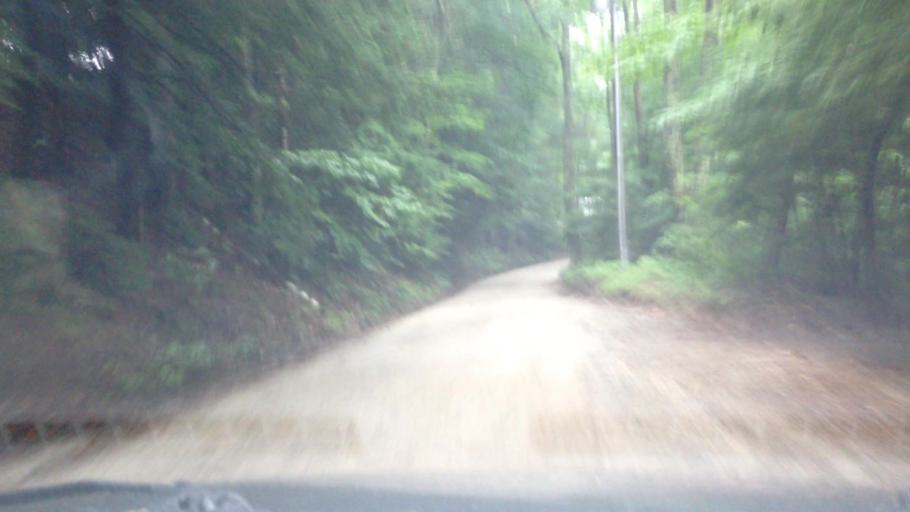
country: US
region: New Hampshire
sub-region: Cheshire County
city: Marlborough
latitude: 42.8748
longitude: -72.2121
